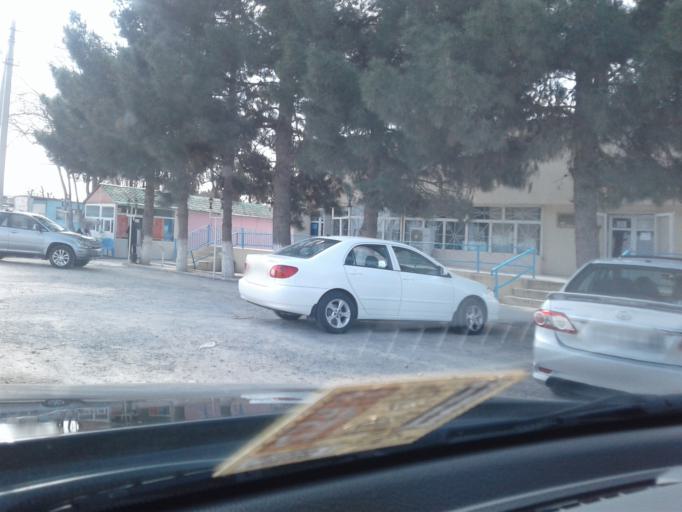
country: TM
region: Ahal
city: Abadan
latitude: 38.1227
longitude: 58.3489
